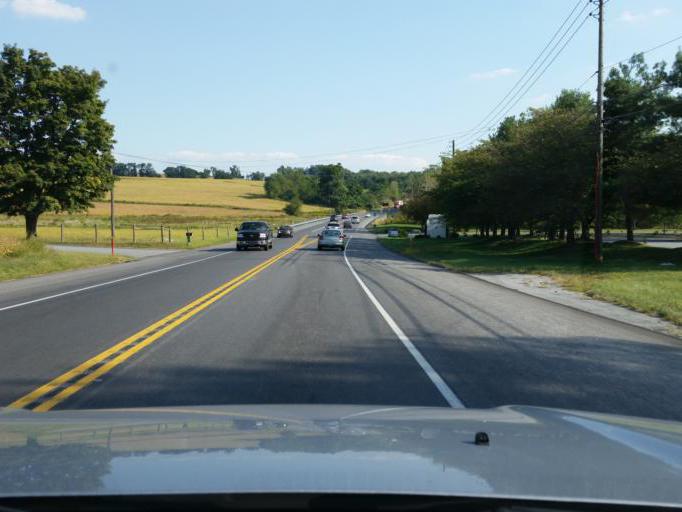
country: US
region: Pennsylvania
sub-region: Lancaster County
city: Gap
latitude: 39.9739
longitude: -76.0080
